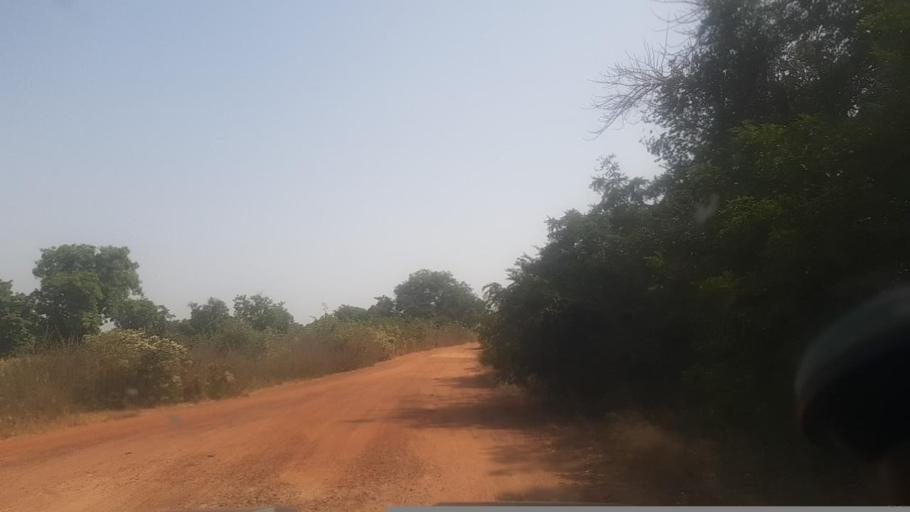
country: ML
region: Segou
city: Bla
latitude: 12.9209
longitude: -6.2593
